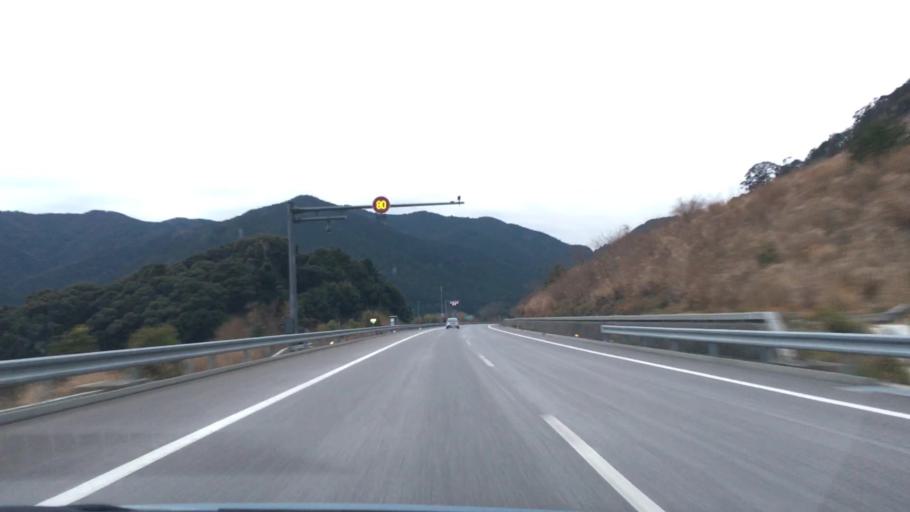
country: JP
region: Aichi
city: Shinshiro
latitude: 34.8435
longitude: 137.6074
